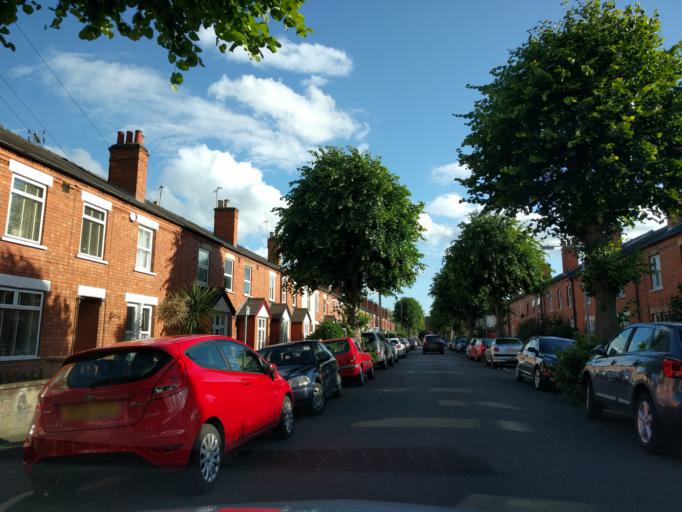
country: GB
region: England
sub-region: Nottinghamshire
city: Newark on Trent
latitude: 53.0696
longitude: -0.8084
